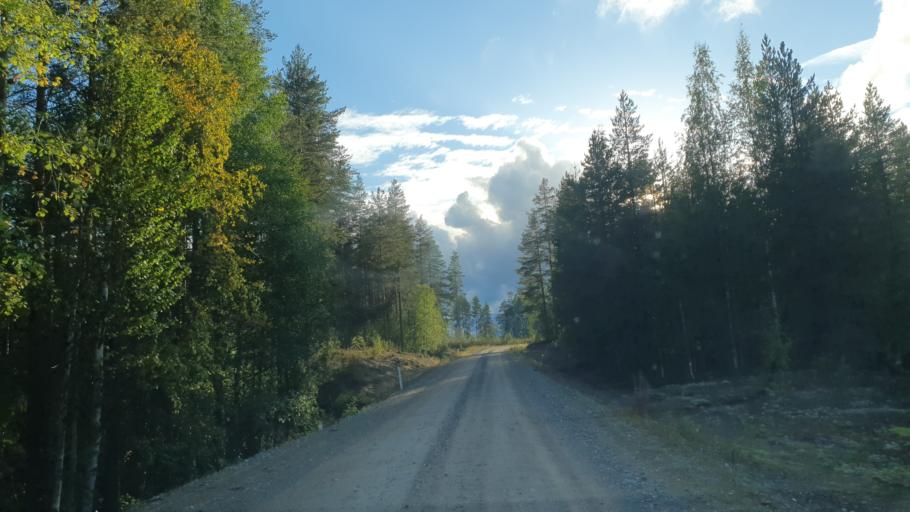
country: FI
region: Kainuu
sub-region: Kehys-Kainuu
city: Kuhmo
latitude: 64.3367
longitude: 29.9615
